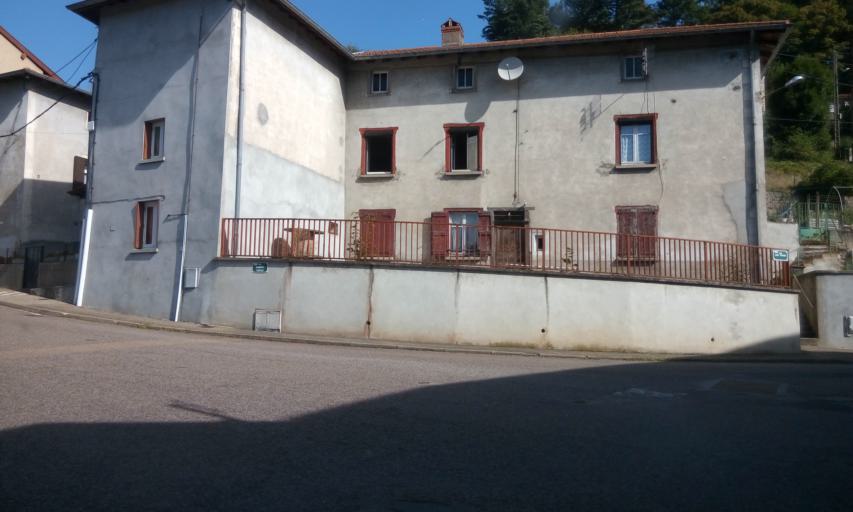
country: FR
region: Rhone-Alpes
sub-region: Departement du Rhone
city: Amplepuis
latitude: 45.9742
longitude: 4.3272
